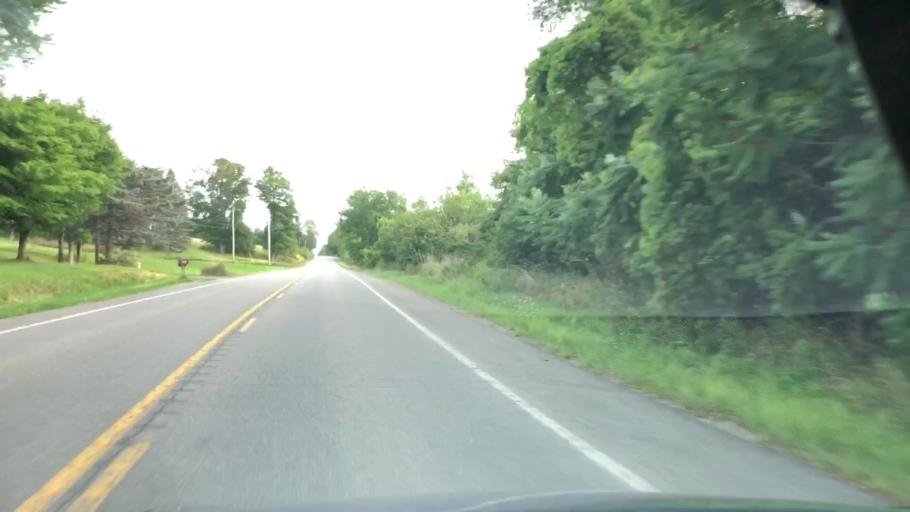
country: US
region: Pennsylvania
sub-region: Erie County
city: Union City
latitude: 41.8502
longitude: -79.8242
